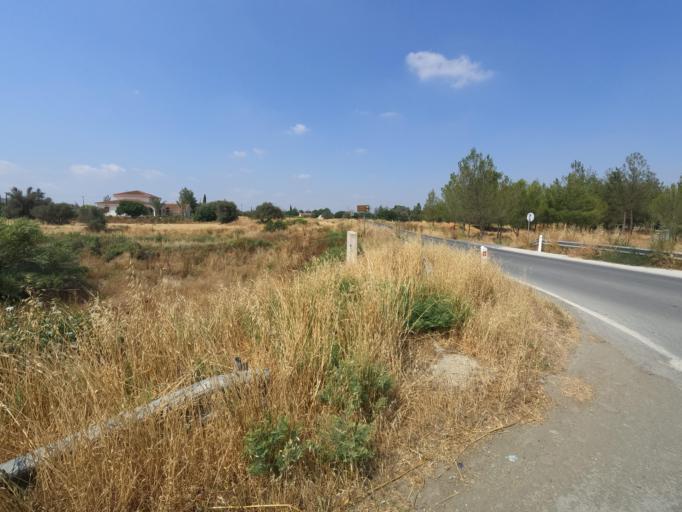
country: CY
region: Lefkosia
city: Dali
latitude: 35.0367
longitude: 33.4346
